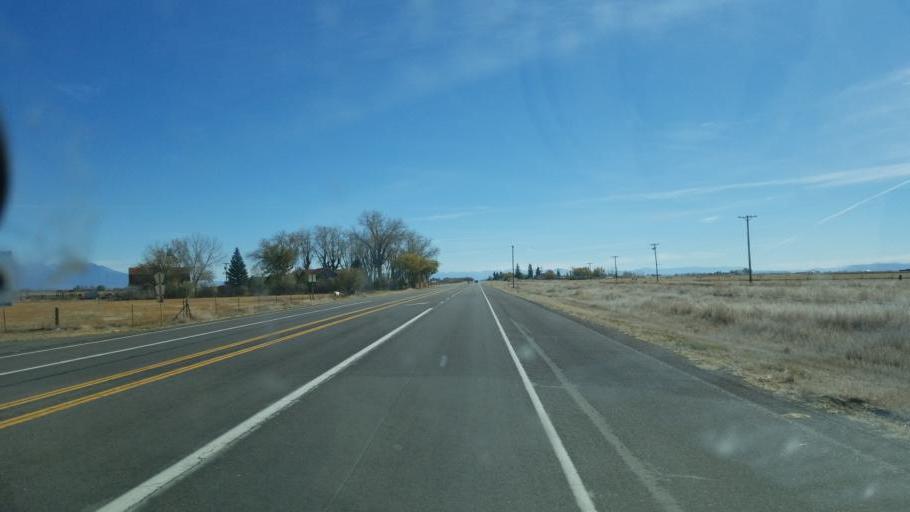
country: US
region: Colorado
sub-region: Rio Grande County
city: Monte Vista
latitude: 37.5594
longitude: -106.0934
